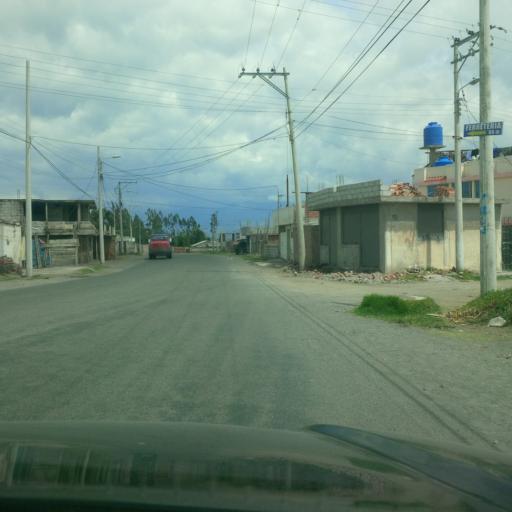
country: EC
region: Chimborazo
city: Riobamba
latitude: -1.6440
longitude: -78.6667
